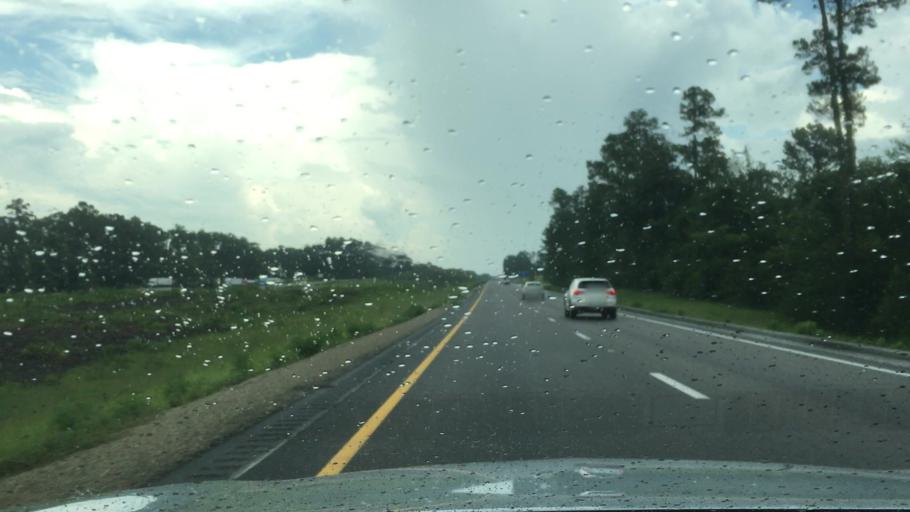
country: US
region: Mississippi
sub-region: Lamar County
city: Purvis
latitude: 31.1968
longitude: -89.3391
